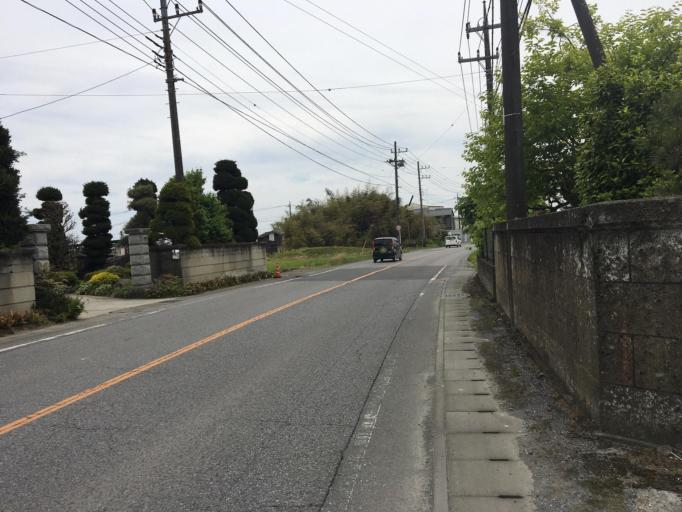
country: JP
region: Tochigi
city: Mibu
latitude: 36.4500
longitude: 139.7563
